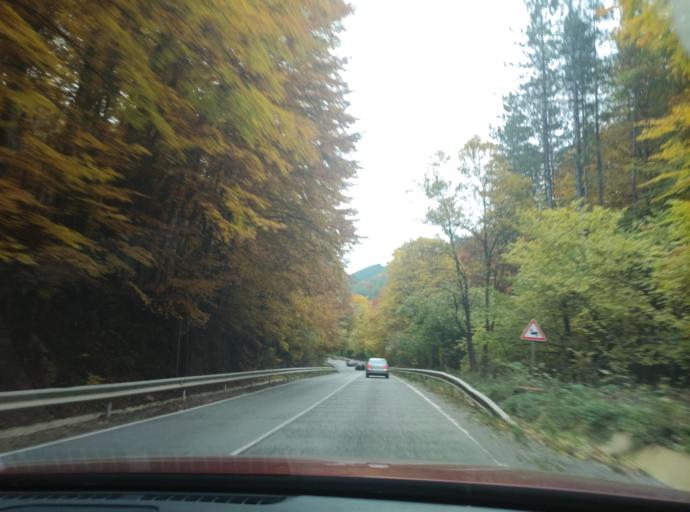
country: BG
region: Sofiya
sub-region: Obshtina Godech
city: Godech
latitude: 43.0232
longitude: 23.1369
